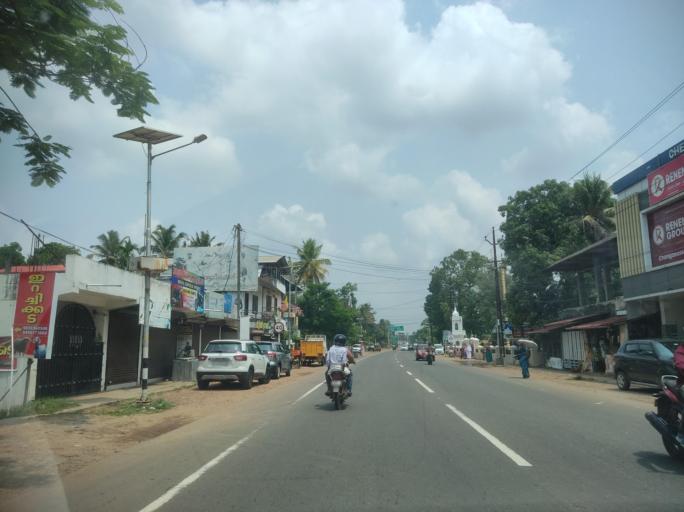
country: IN
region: Kerala
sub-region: Kottayam
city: Changanacheri
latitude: 9.4269
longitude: 76.5457
